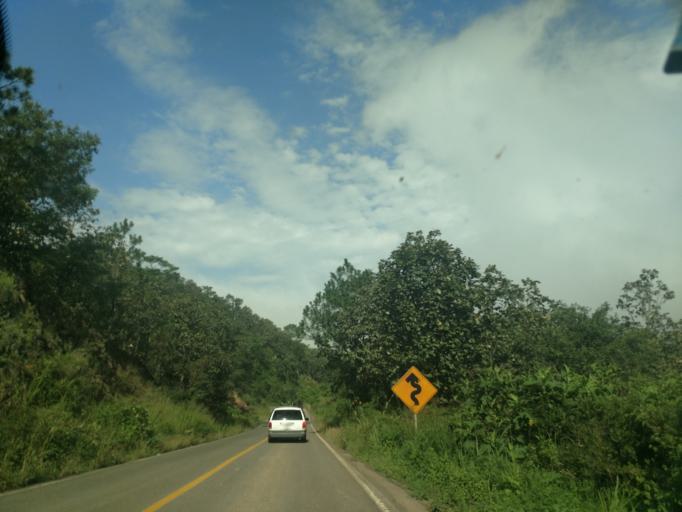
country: MX
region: Jalisco
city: El Salto
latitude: 20.4620
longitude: -104.3819
